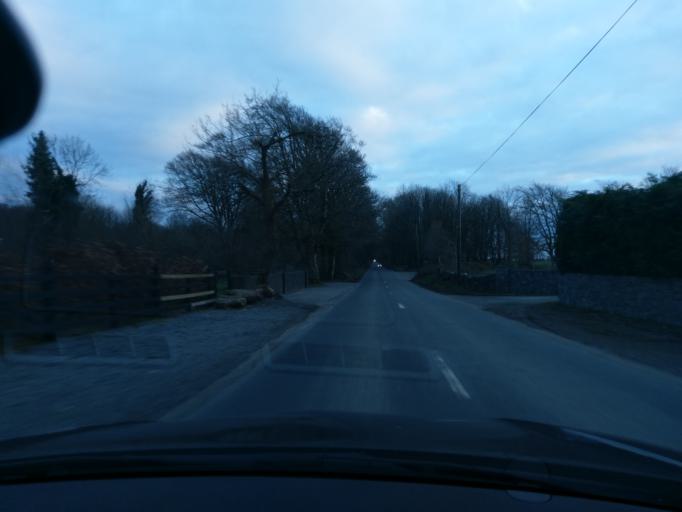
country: IE
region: Connaught
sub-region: County Galway
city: Athenry
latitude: 53.3396
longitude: -8.7735
